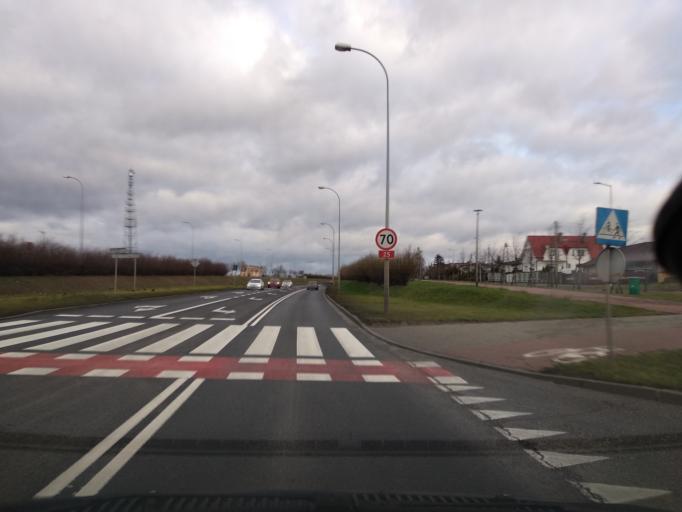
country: PL
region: Greater Poland Voivodeship
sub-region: Kalisz
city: Kalisz
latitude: 51.7783
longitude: 18.0796
